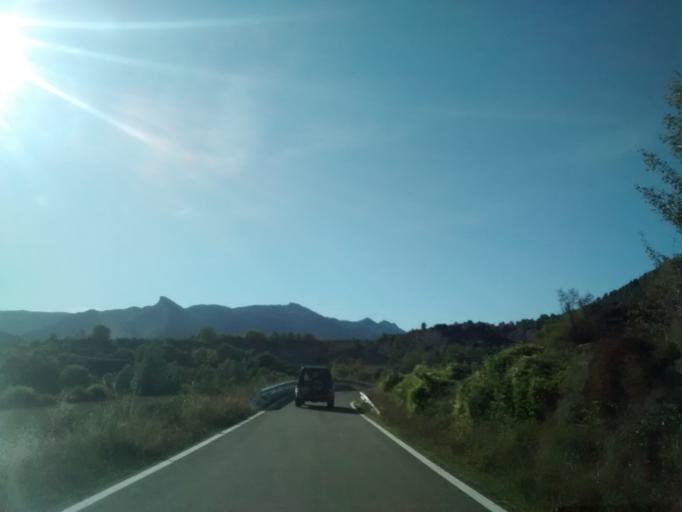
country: ES
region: Aragon
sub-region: Provincia de Huesca
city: Loarre
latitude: 42.3888
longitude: -0.7101
